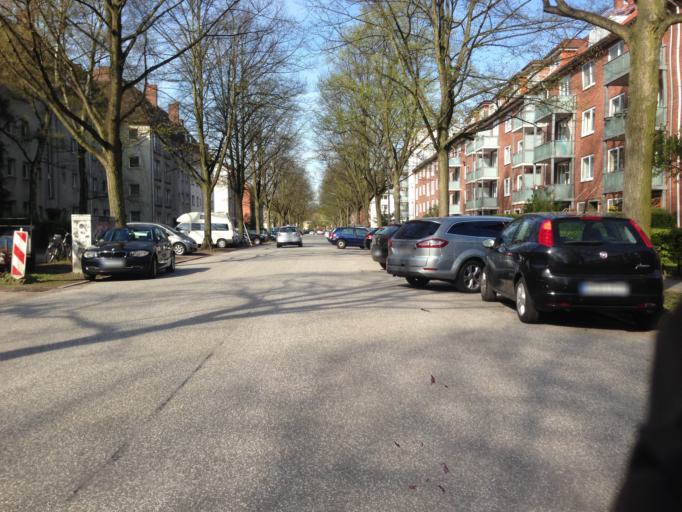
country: DE
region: Hamburg
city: Borgfelde
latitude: 53.5643
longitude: 10.0499
